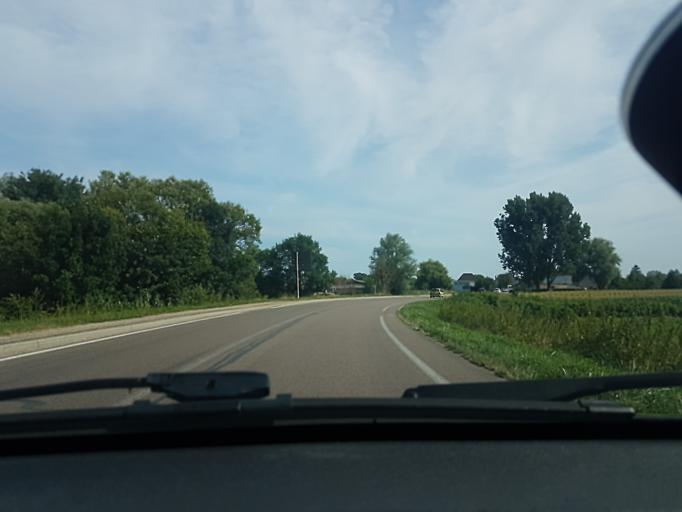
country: FR
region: Bourgogne
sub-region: Departement de Saone-et-Loire
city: Epervans
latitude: 46.7601
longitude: 4.8945
